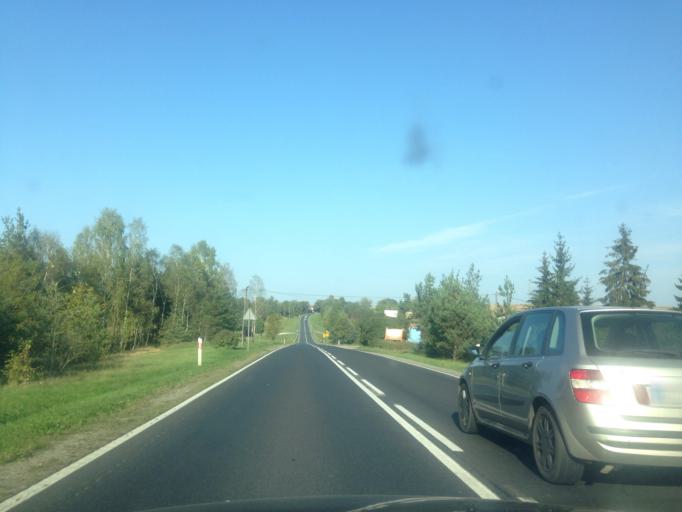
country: PL
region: Kujawsko-Pomorskie
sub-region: Powiat brodnicki
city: Brzozie
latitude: 53.3211
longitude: 19.5340
